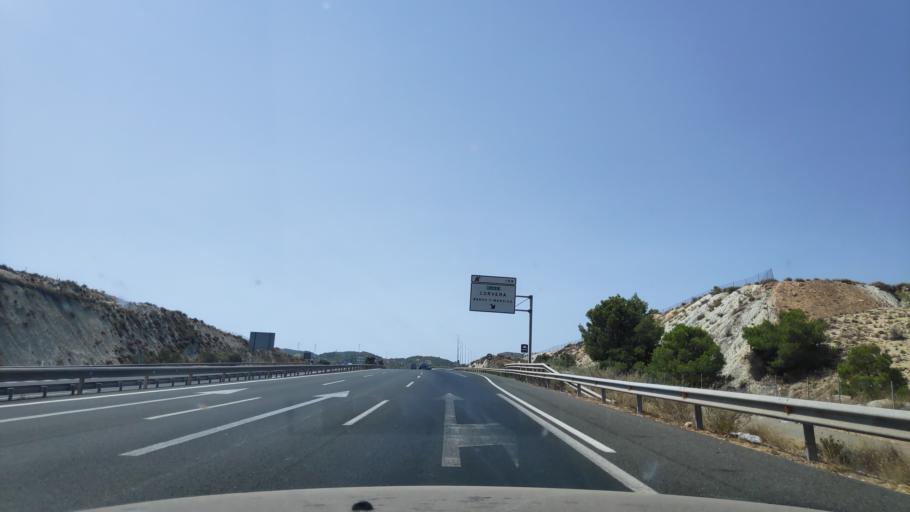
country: ES
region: Murcia
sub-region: Murcia
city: Murcia
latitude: 37.8808
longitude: -1.1325
